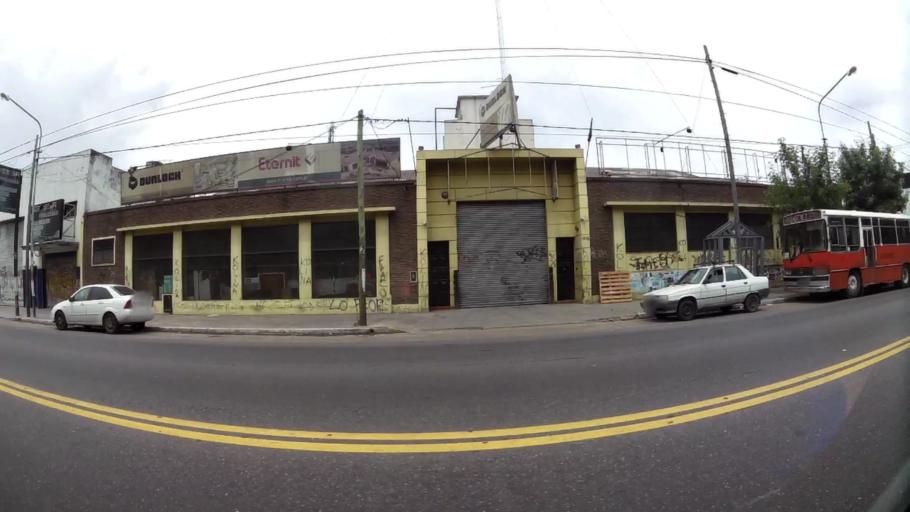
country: AR
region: Buenos Aires
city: San Justo
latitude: -34.6698
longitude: -58.5358
